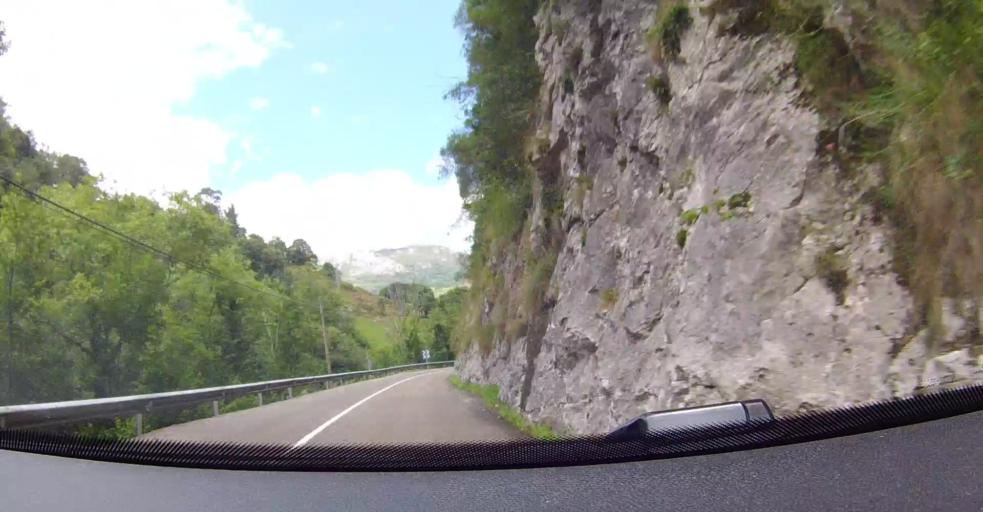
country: ES
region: Cantabria
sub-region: Provincia de Cantabria
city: Tresviso
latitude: 43.3138
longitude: -4.6088
